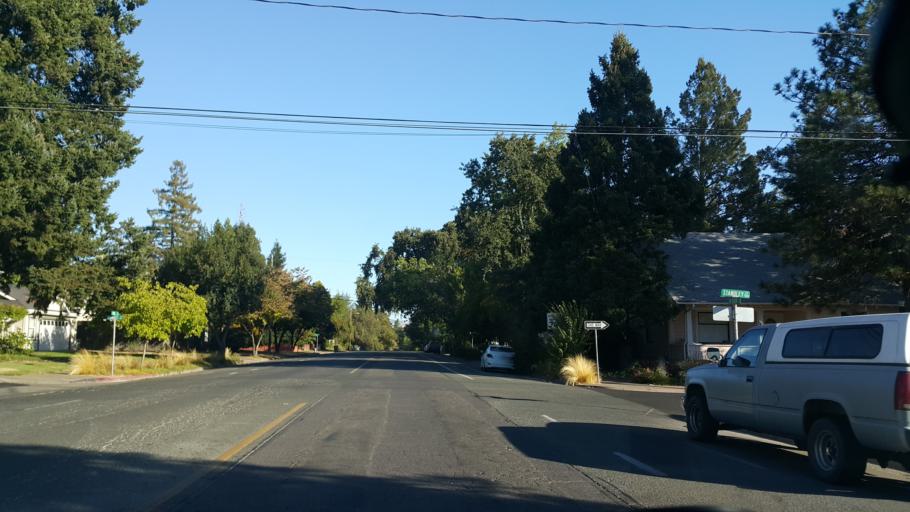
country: US
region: California
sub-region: Mendocino County
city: Ukiah
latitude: 39.1497
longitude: -123.2126
